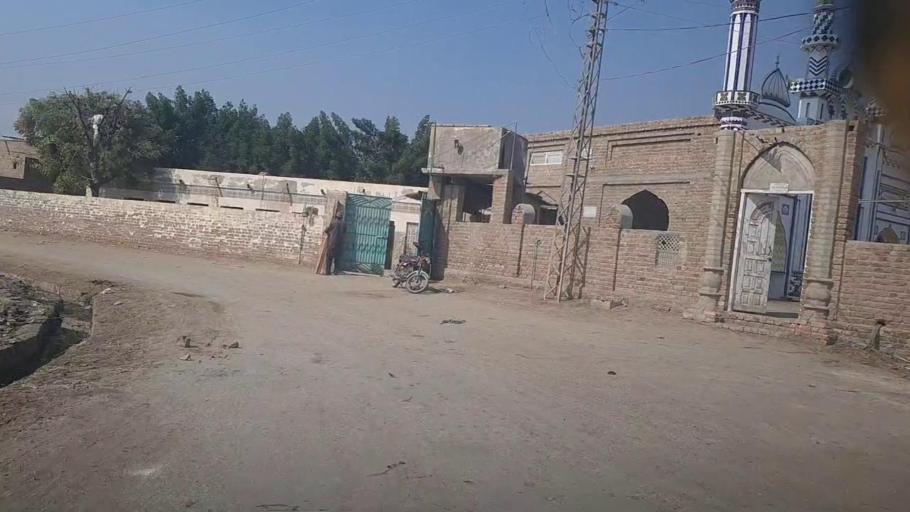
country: PK
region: Sindh
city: Khairpur
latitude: 27.5526
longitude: 68.7820
